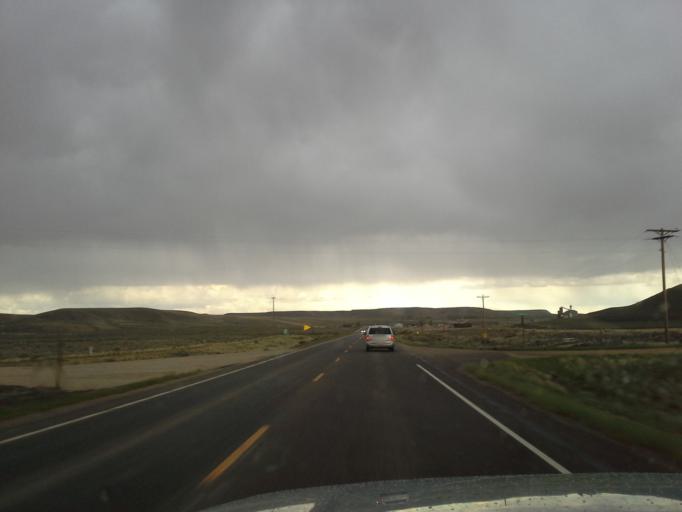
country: US
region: Wyoming
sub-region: Park County
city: Powell
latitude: 45.0644
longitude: -108.6670
